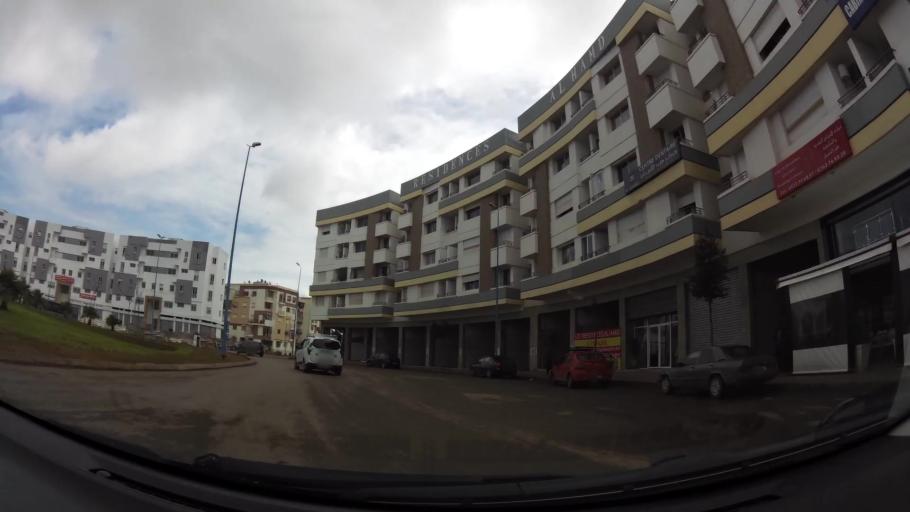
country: MA
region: Grand Casablanca
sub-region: Casablanca
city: Casablanca
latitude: 33.5386
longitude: -7.6933
